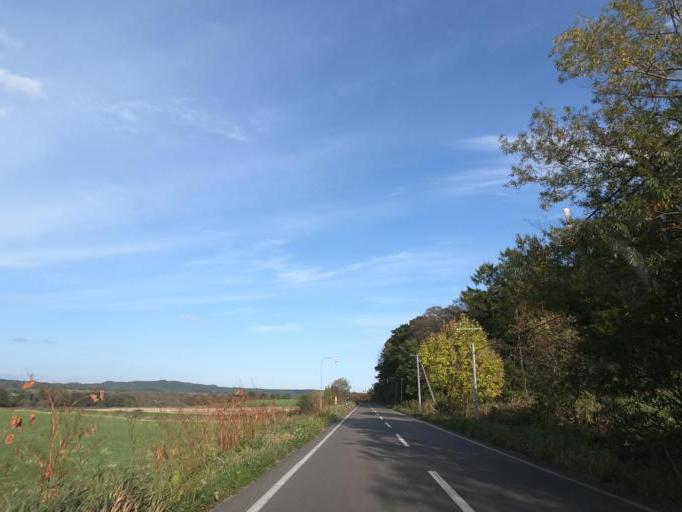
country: JP
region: Hokkaido
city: Obihiro
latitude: 42.5595
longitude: 143.3390
